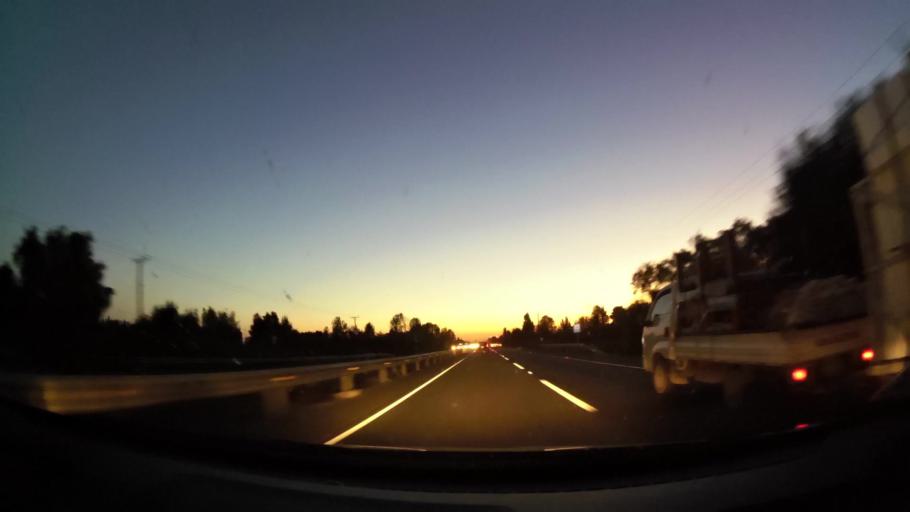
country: CL
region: Biobio
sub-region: Provincia de Nuble
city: San Carlos
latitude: -36.3474
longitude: -71.8557
